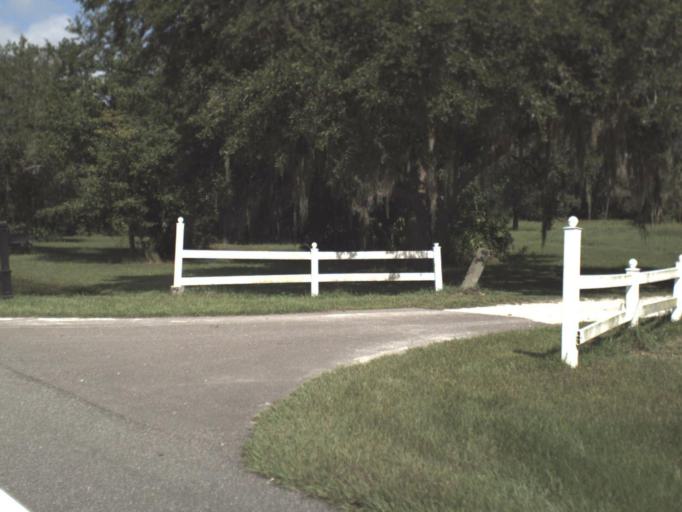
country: US
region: Florida
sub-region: Sarasota County
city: Lake Sarasota
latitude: 27.2646
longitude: -82.4122
